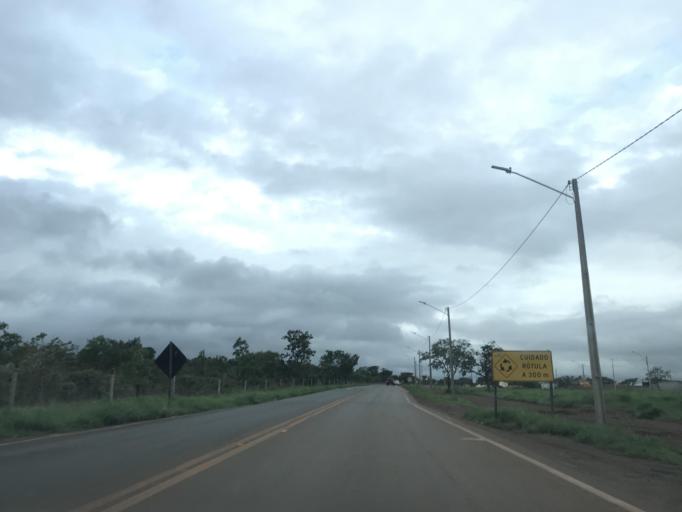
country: BR
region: Goias
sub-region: Luziania
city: Luziania
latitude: -16.2639
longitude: -47.9753
